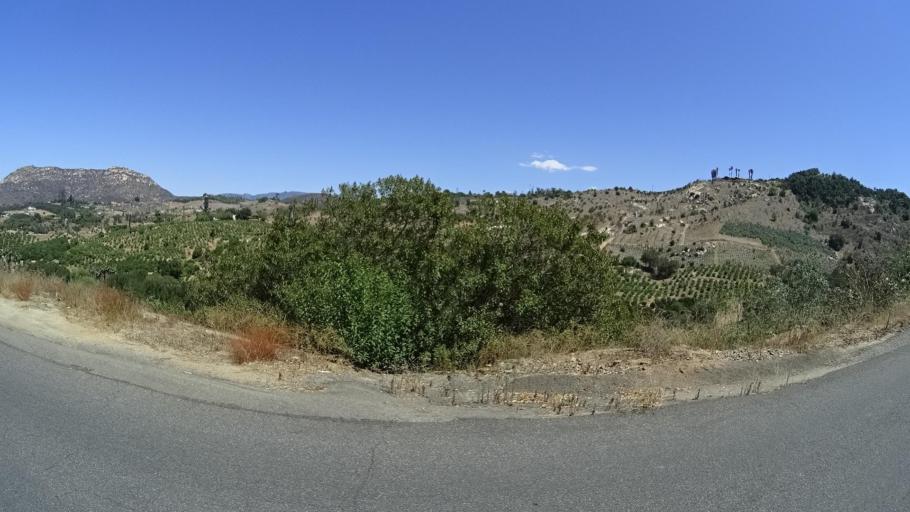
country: US
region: California
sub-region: San Diego County
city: Hidden Meadows
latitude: 33.3126
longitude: -117.0980
